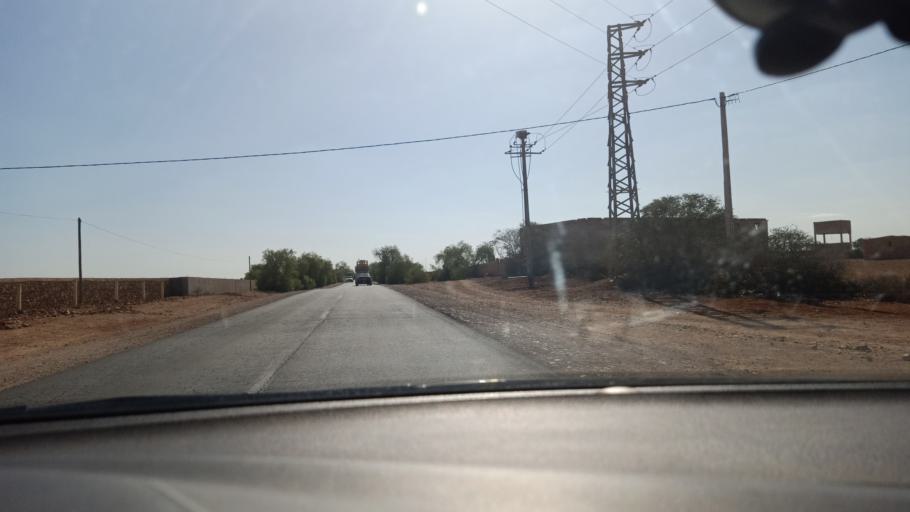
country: MA
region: Doukkala-Abda
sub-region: Safi
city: Youssoufia
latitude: 32.0931
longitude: -8.6161
